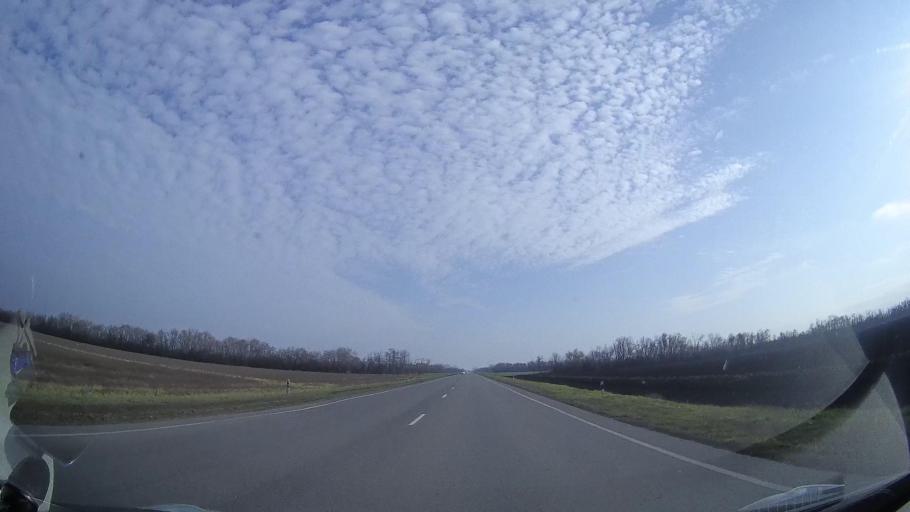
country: RU
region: Rostov
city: Tselina
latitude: 46.5245
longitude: 41.1074
